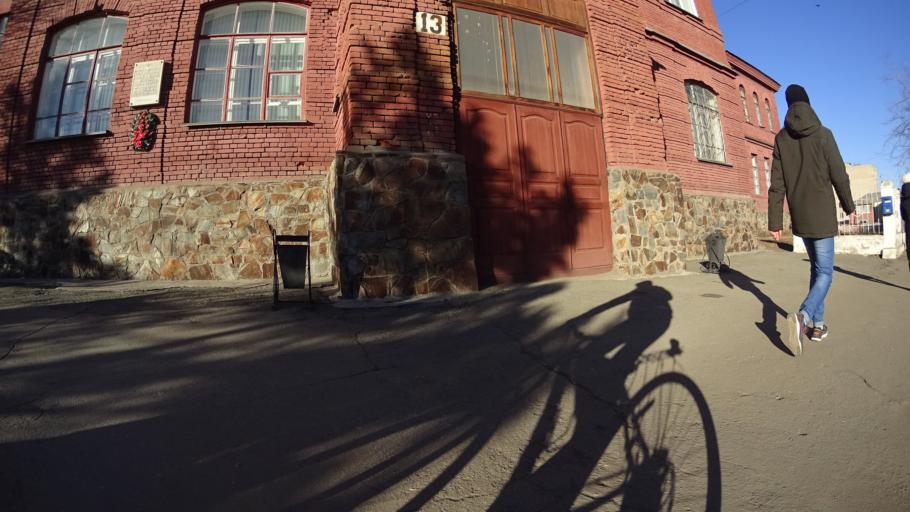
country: RU
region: Chelyabinsk
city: Troitsk
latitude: 54.0845
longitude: 61.5445
